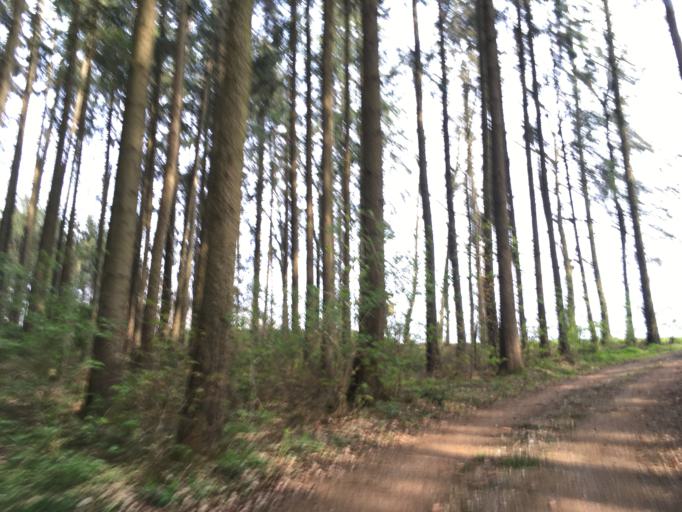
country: DE
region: Bavaria
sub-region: Upper Bavaria
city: Jettenbach
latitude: 48.1591
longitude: 12.3711
